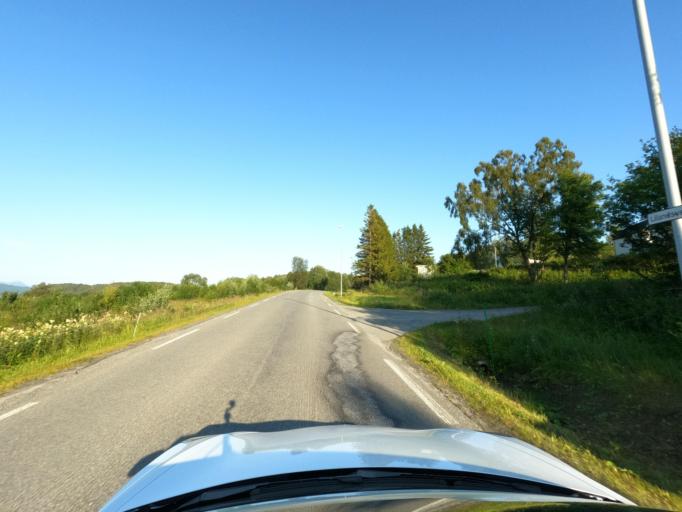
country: NO
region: Nordland
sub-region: Evenes
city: Randa
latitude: 68.4900
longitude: 16.8974
